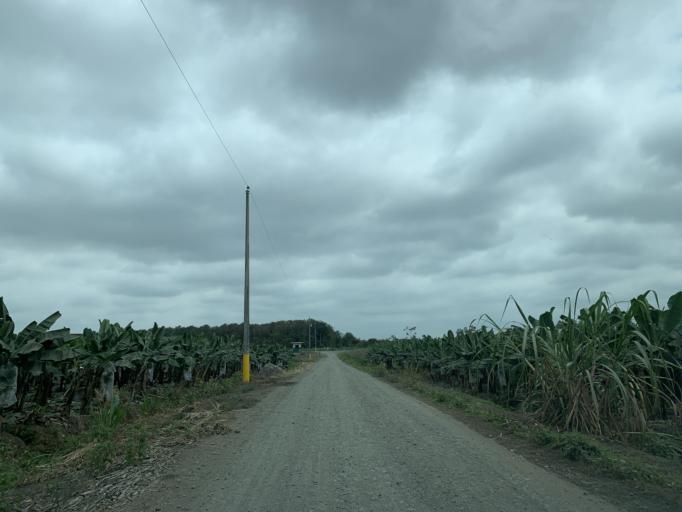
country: EC
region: Guayas
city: Coronel Marcelino Mariduena
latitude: -2.3311
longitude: -79.4544
